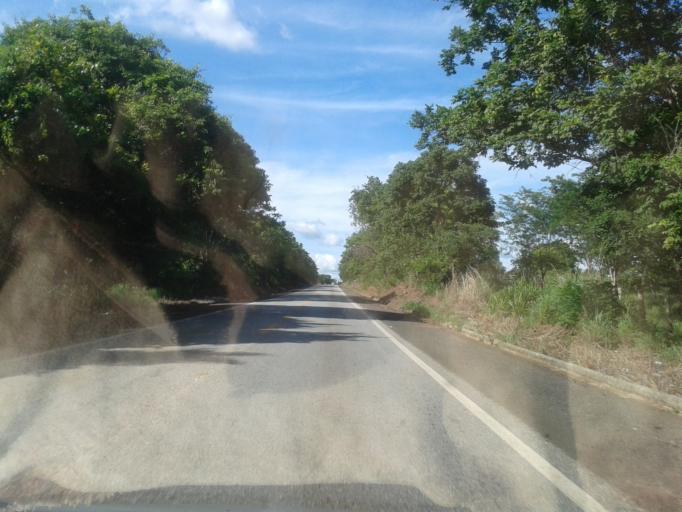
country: BR
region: Goias
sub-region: Mozarlandia
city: Mozarlandia
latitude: -14.9467
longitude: -50.5782
